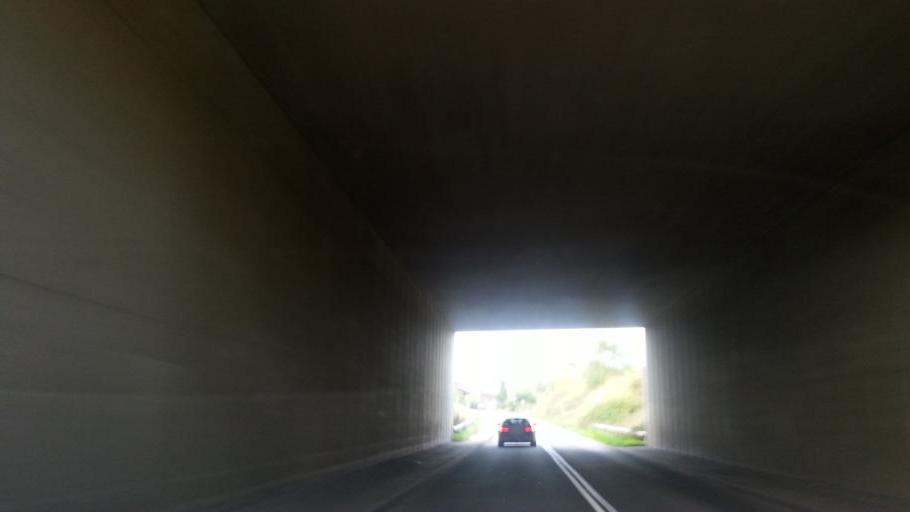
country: GB
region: England
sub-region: City and Borough of Birmingham
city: Sutton Coldfield
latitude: 52.5931
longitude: -1.7955
